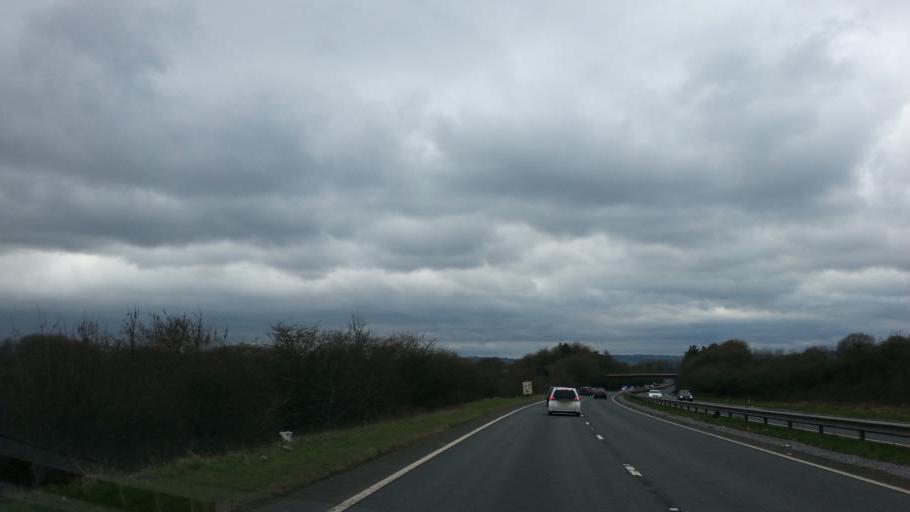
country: GB
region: England
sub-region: Devon
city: Cullompton
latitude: 50.9194
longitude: -3.4074
